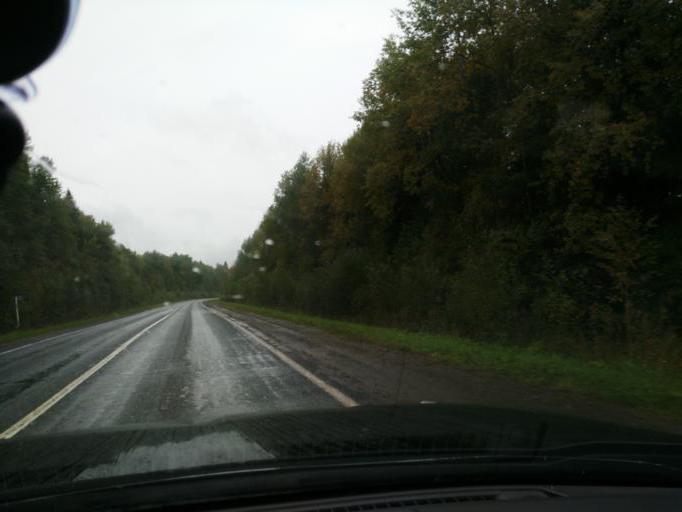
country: RU
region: Perm
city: Yugo-Kamskiy
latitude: 57.6448
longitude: 55.6024
